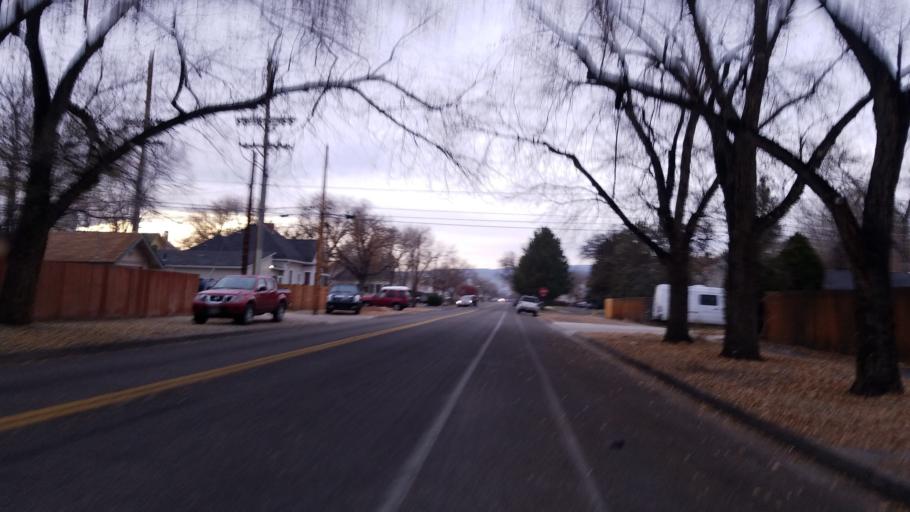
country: US
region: Colorado
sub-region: Mesa County
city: Grand Junction
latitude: 39.0723
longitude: -108.5679
